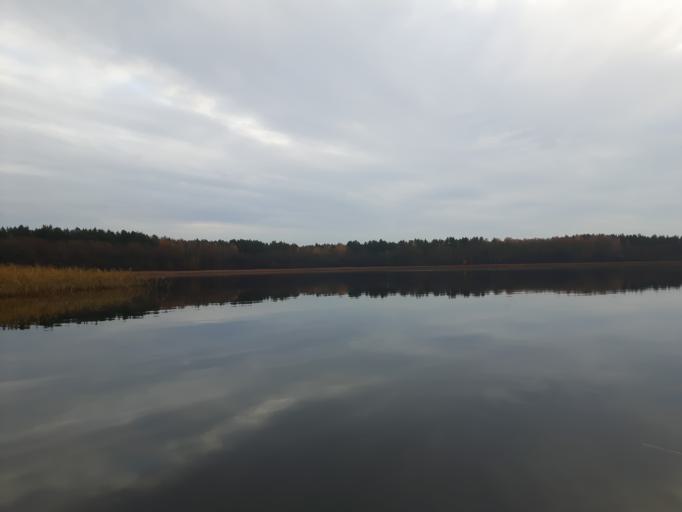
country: PL
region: Warmian-Masurian Voivodeship
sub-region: Powiat olsztynski
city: Barczewo
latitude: 53.8265
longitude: 20.7389
